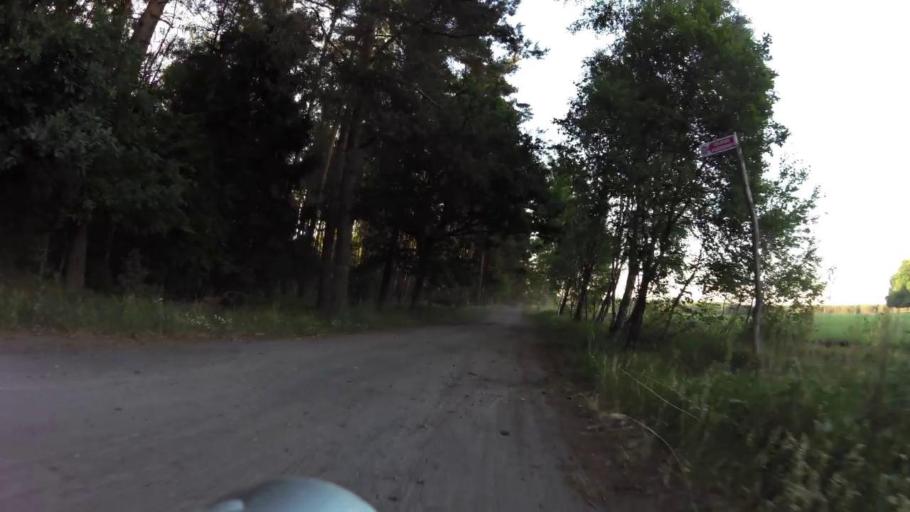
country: PL
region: West Pomeranian Voivodeship
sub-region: Powiat szczecinecki
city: Szczecinek
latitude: 53.8138
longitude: 16.6963
